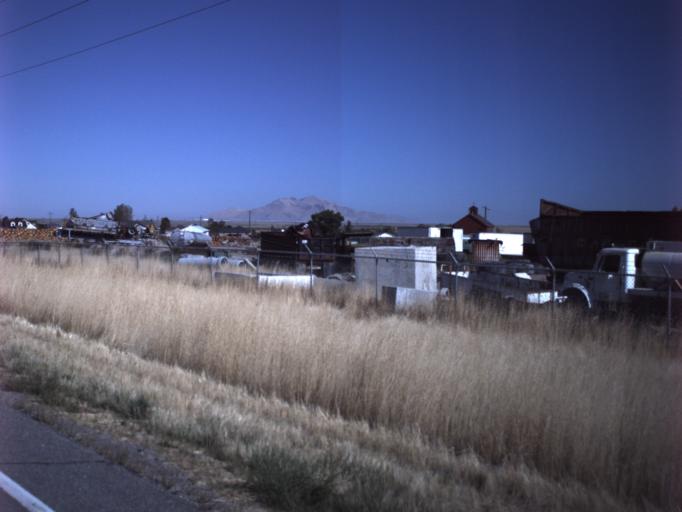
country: US
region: Utah
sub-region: Tooele County
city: Grantsville
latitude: 40.6063
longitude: -112.4887
